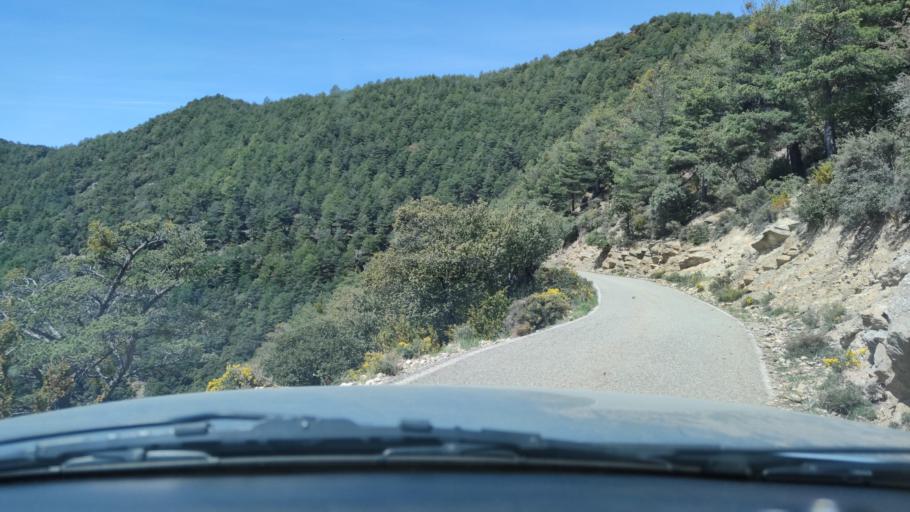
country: ES
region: Catalonia
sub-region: Provincia de Lleida
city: Sort
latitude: 42.3109
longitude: 1.1318
